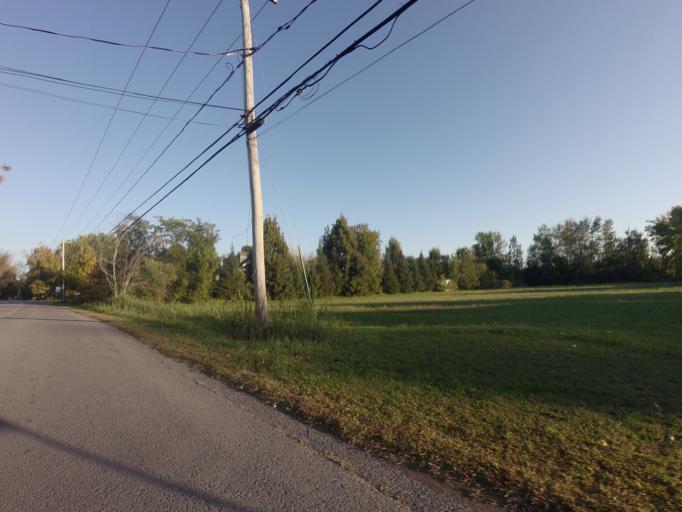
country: CA
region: Quebec
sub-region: Monteregie
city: Rigaud
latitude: 45.4789
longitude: -74.2406
